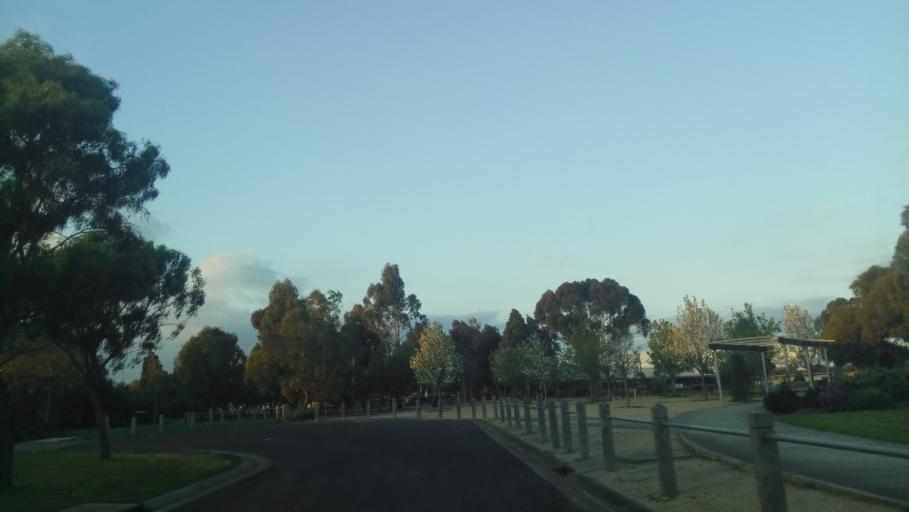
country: AU
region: Victoria
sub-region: Hobsons Bay
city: Altona Meadows
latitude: -37.8789
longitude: 144.7822
